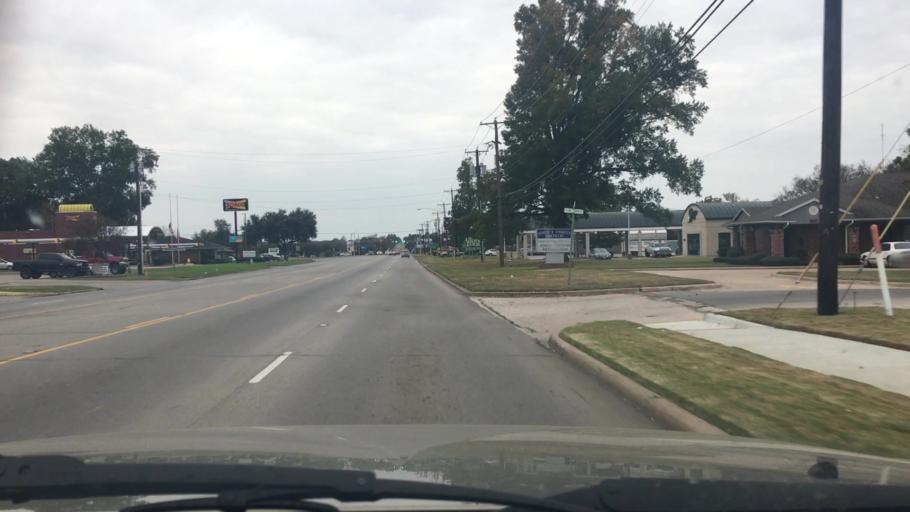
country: US
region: Texas
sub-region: Hopkins County
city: Sulphur Springs
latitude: 33.1123
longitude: -95.5968
